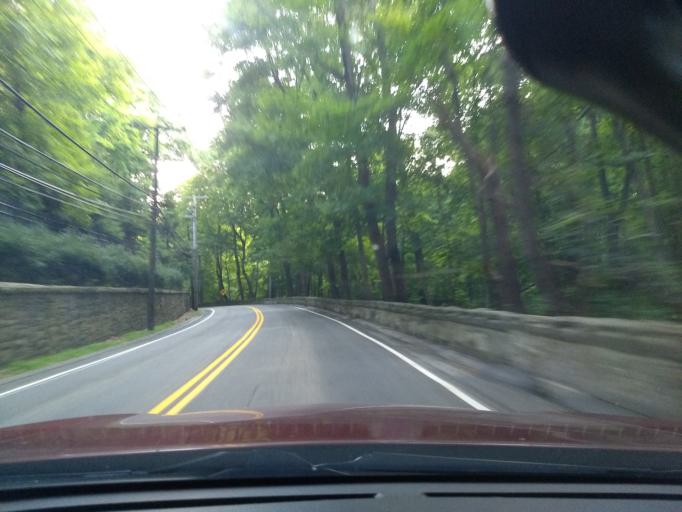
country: US
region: Pennsylvania
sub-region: Allegheny County
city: Sewickley
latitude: 40.5501
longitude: -80.1688
